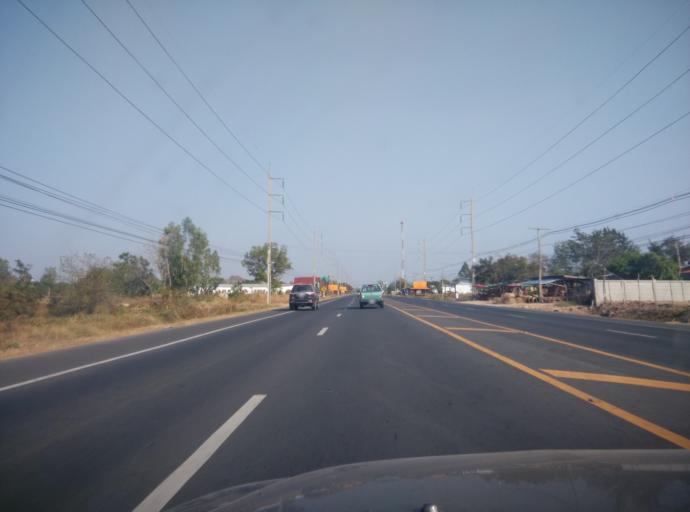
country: TH
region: Sisaket
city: Uthumphon Phisai
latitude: 15.1575
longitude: 104.1795
